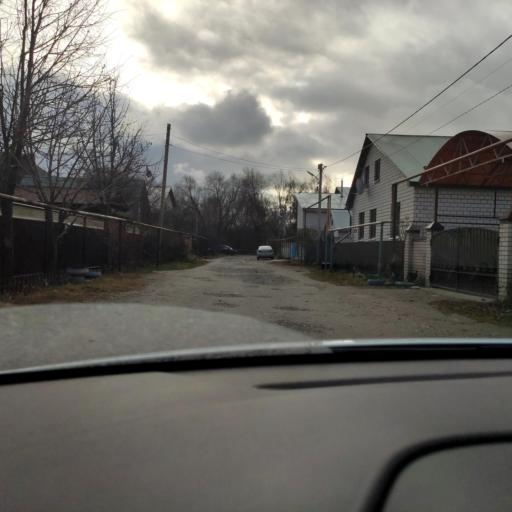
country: RU
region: Tatarstan
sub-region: Gorod Kazan'
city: Kazan
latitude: 55.8817
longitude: 49.0991
